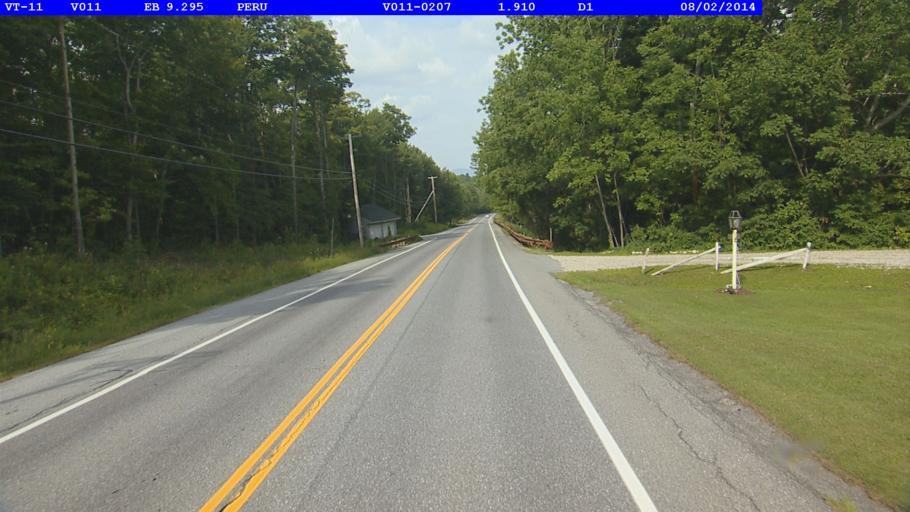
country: US
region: Vermont
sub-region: Bennington County
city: Manchester Center
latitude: 43.2230
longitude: -72.9122
